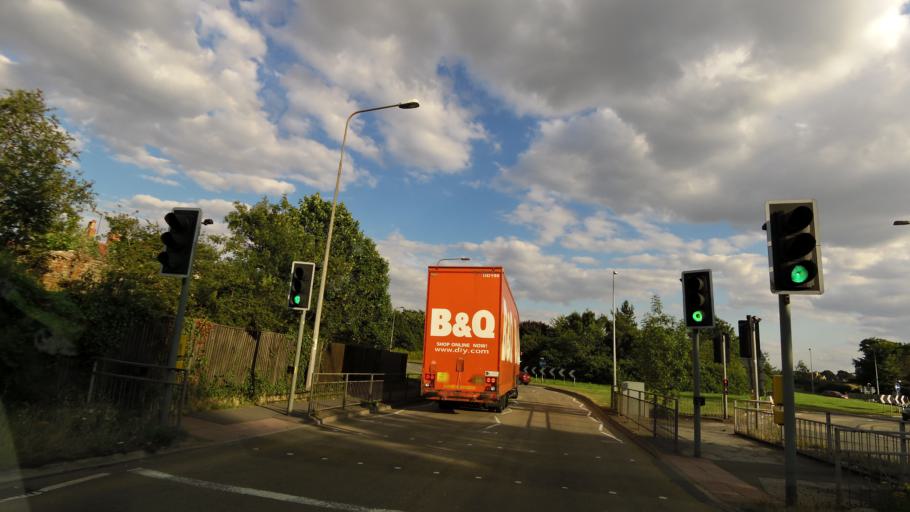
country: GB
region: England
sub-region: Nottinghamshire
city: Worksop
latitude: 53.3033
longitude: -1.1370
